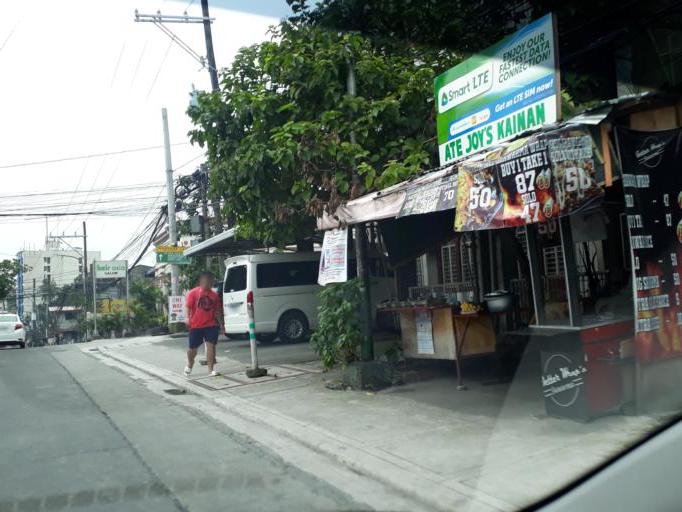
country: PH
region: Metro Manila
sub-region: Quezon City
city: Quezon City
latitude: 14.6278
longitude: 121.0389
